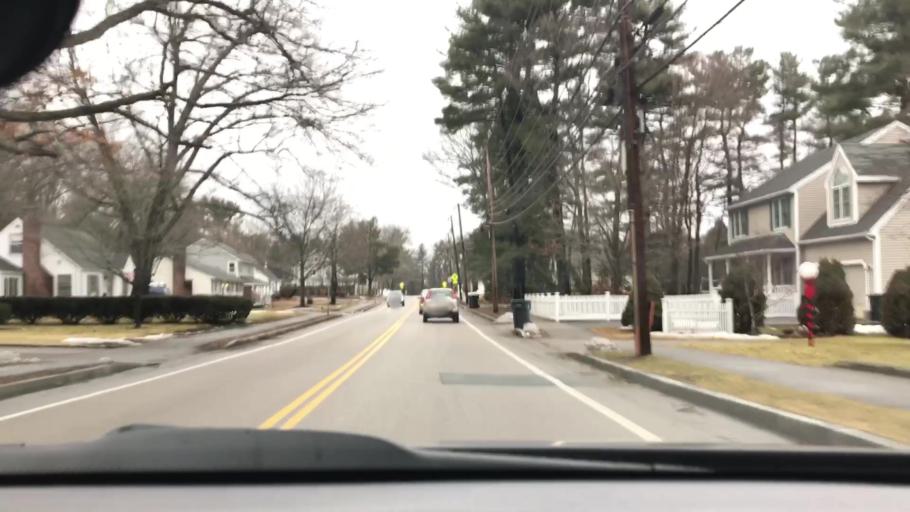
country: US
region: Massachusetts
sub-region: Middlesex County
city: Natick
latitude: 42.3081
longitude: -71.3332
